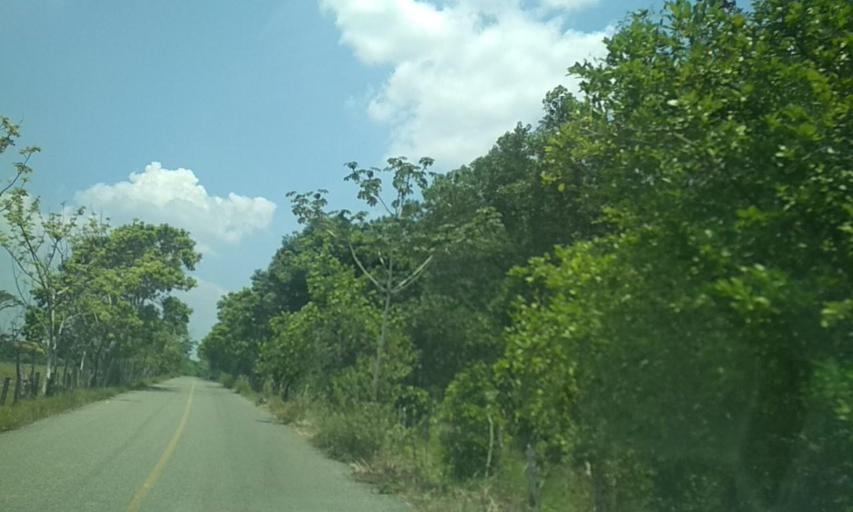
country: MX
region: Tabasco
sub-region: Huimanguillo
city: Francisco Rueda
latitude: 17.8368
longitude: -93.9125
